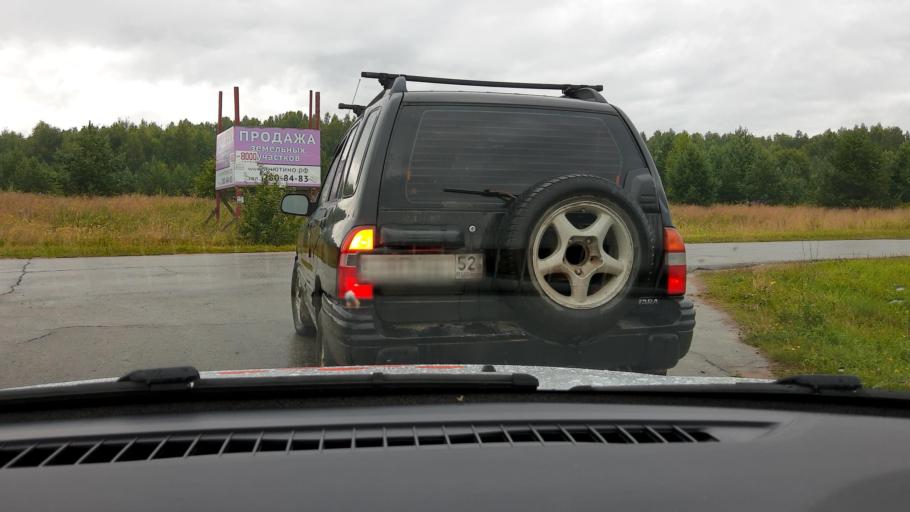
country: RU
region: Nizjnij Novgorod
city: Surovatikha
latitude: 55.9444
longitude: 43.9159
